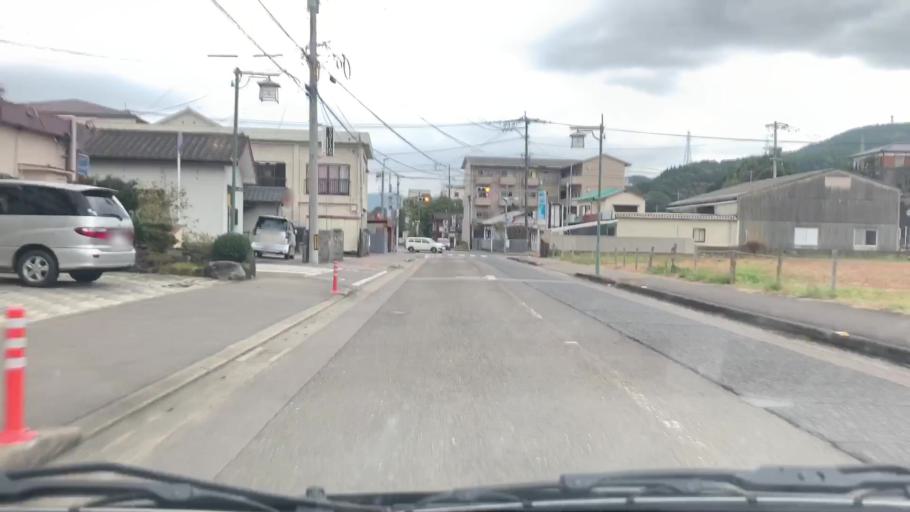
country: JP
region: Saga Prefecture
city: Ureshinomachi-shimojuku
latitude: 33.0931
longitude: 129.9825
